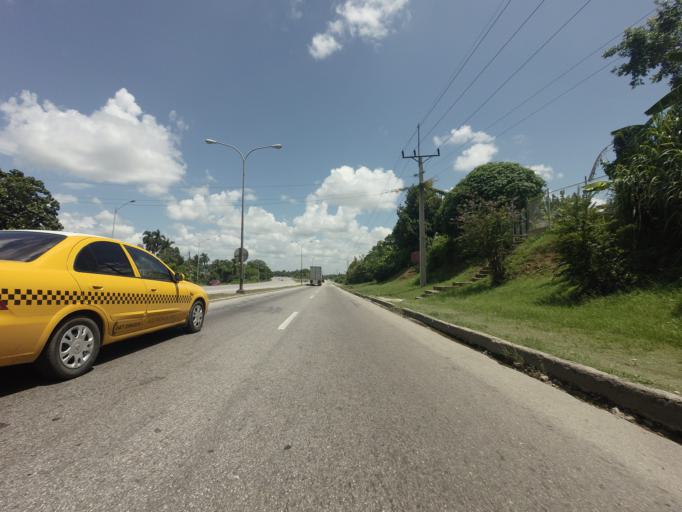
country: CU
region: La Habana
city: Arroyo Naranjo
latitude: 23.0406
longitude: -82.3619
